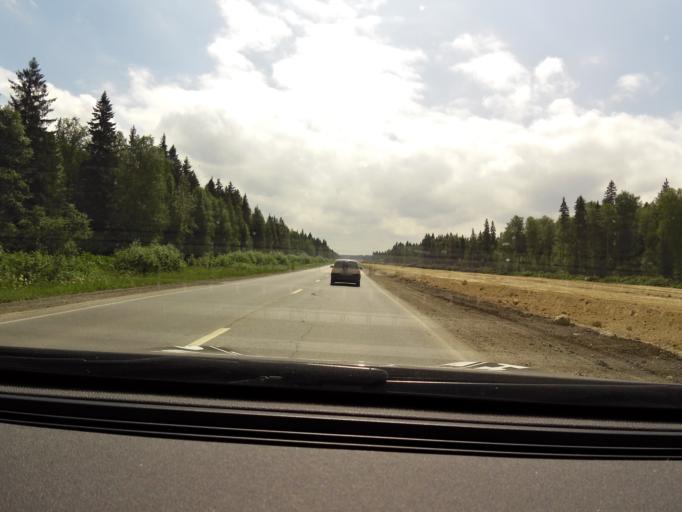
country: RU
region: Perm
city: Kukushtan
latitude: 57.6621
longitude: 56.4393
